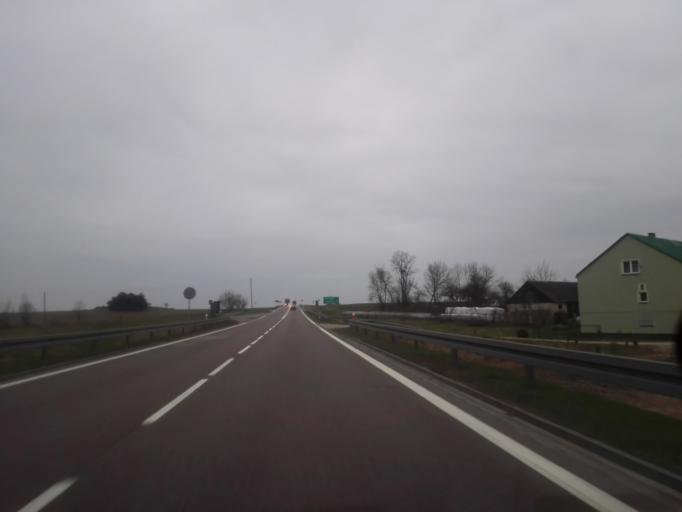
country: PL
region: Podlasie
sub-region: Powiat grajewski
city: Szczuczyn
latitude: 53.5132
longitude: 22.2442
